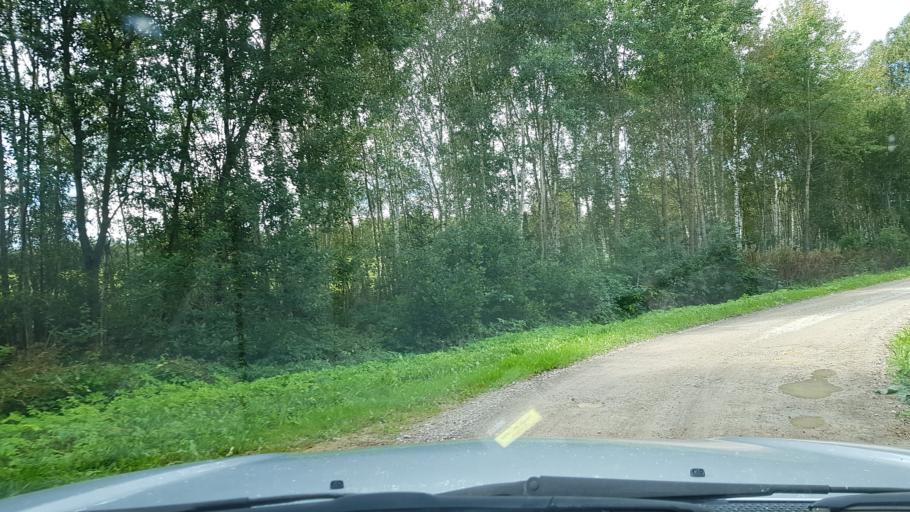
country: EE
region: Harju
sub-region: Raasiku vald
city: Arukula
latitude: 59.3007
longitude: 25.0722
